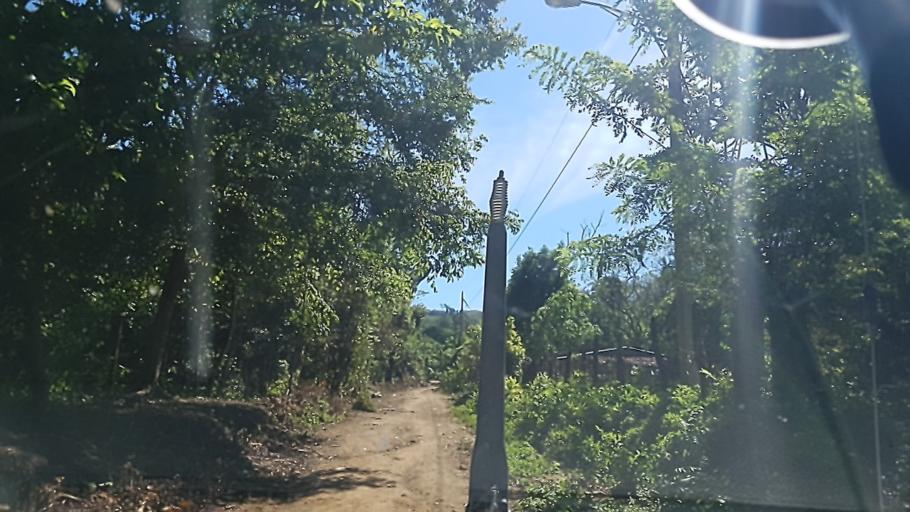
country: NI
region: Carazo
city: Santa Teresa
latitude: 11.6696
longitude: -86.1735
